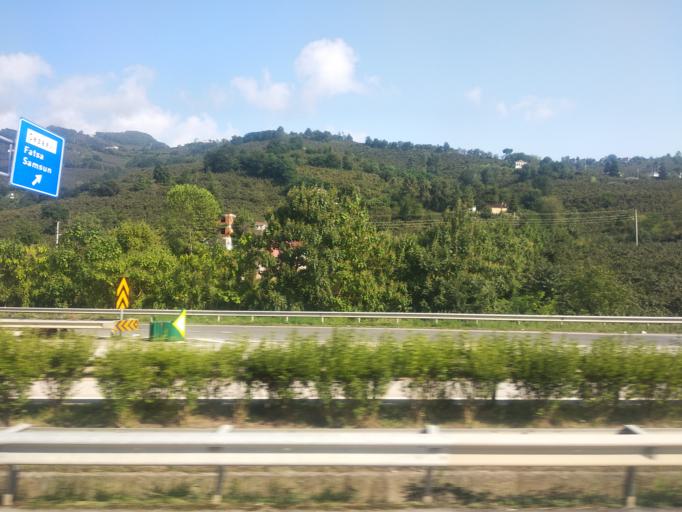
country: TR
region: Ordu
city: Ordu
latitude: 41.0051
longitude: 37.8272
